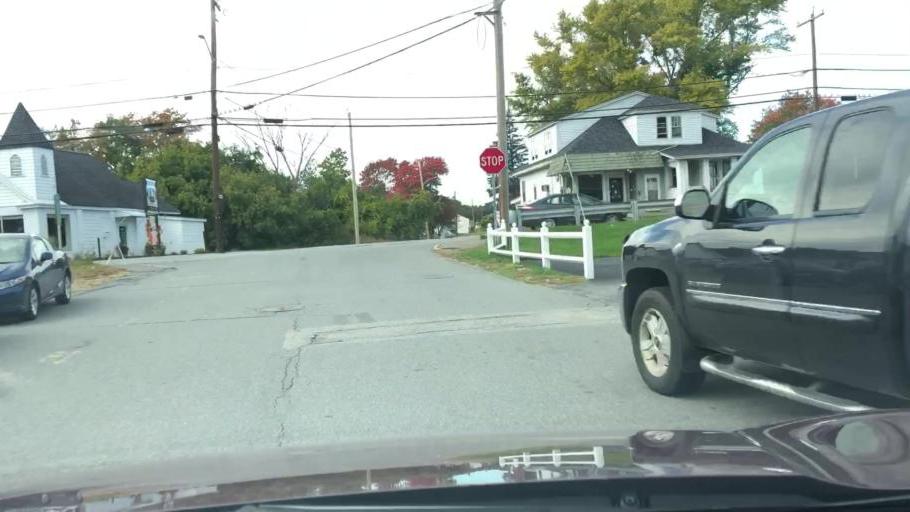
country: US
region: Massachusetts
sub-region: Essex County
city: North Andover
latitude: 42.7365
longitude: -71.1331
